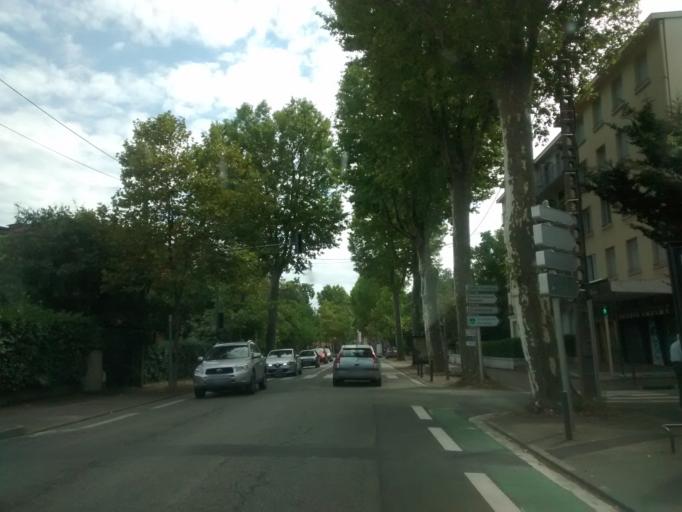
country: FR
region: Midi-Pyrenees
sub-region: Departement de la Haute-Garonne
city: L'Union
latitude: 43.6388
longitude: 1.4653
